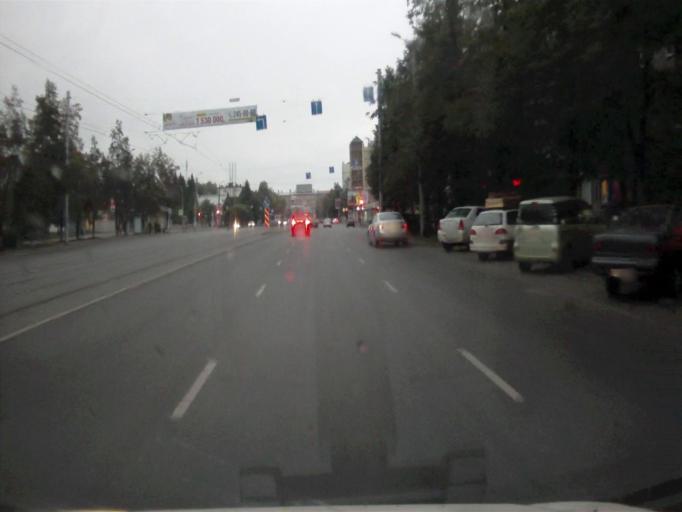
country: RU
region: Chelyabinsk
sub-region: Gorod Chelyabinsk
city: Chelyabinsk
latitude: 55.1781
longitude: 61.3996
